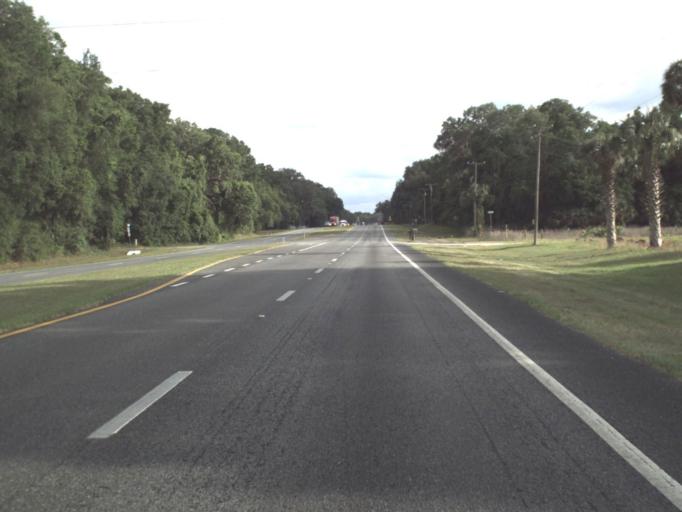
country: US
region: Florida
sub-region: Marion County
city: Citra
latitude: 29.4271
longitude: -82.1100
